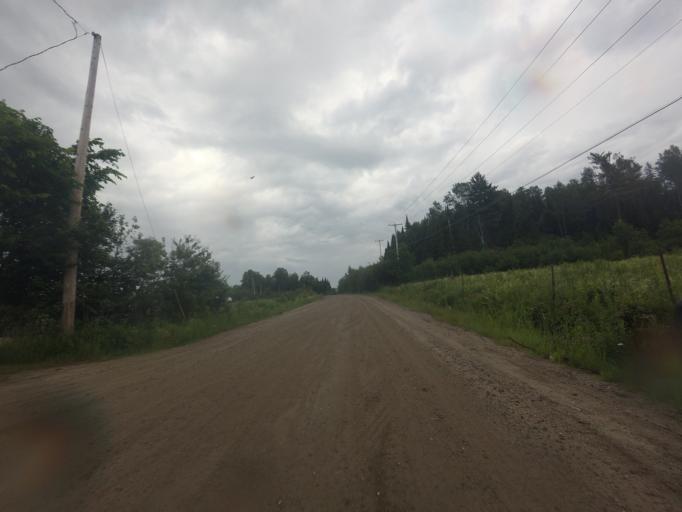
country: CA
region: Quebec
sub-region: Outaouais
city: Maniwaki
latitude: 46.4483
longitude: -75.9385
